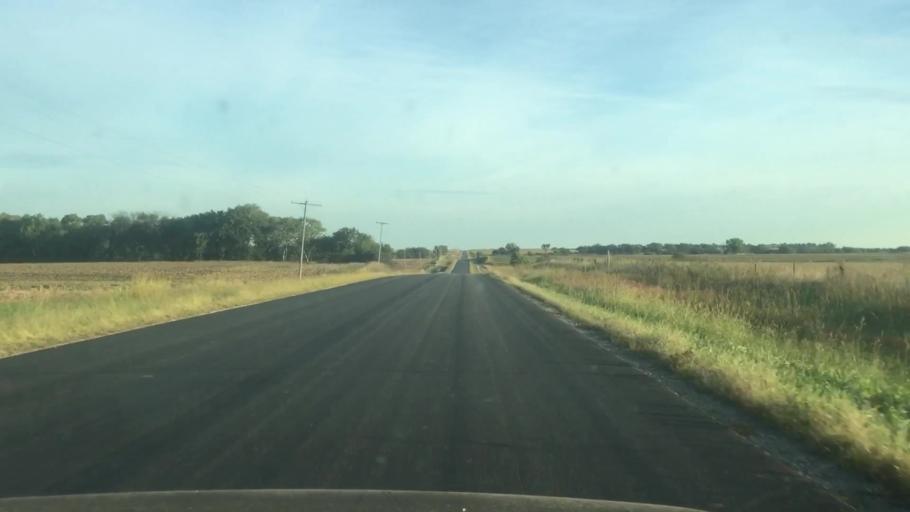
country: US
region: Kansas
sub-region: Marshall County
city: Marysville
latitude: 39.8738
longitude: -96.6009
